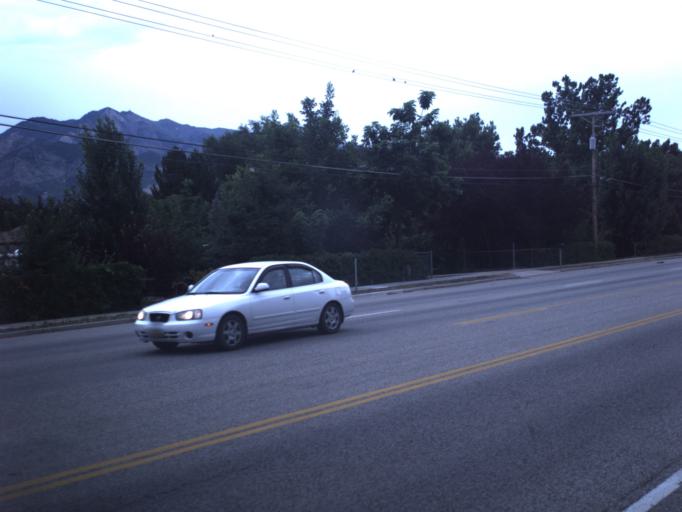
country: US
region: Utah
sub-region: Weber County
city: Harrisville
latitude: 41.2622
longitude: -111.9779
